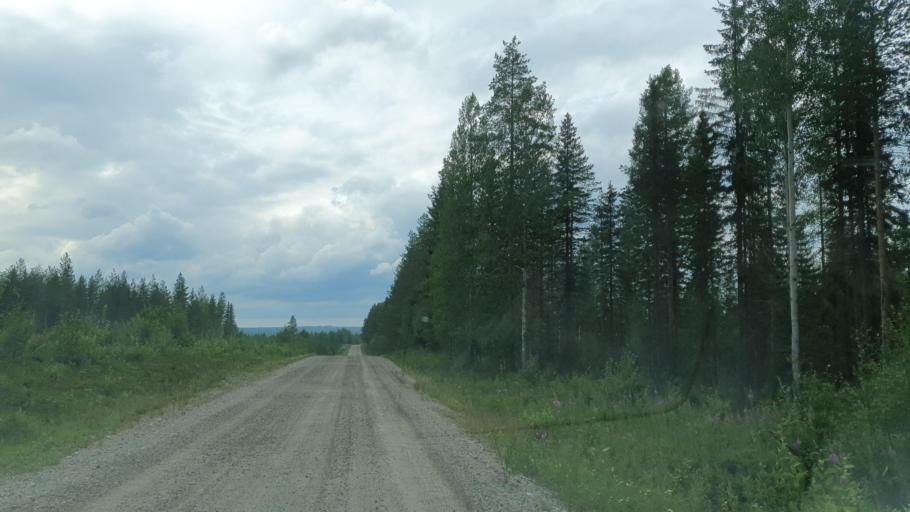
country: FI
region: Kainuu
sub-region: Kehys-Kainuu
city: Kuhmo
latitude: 64.4872
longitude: 29.7221
